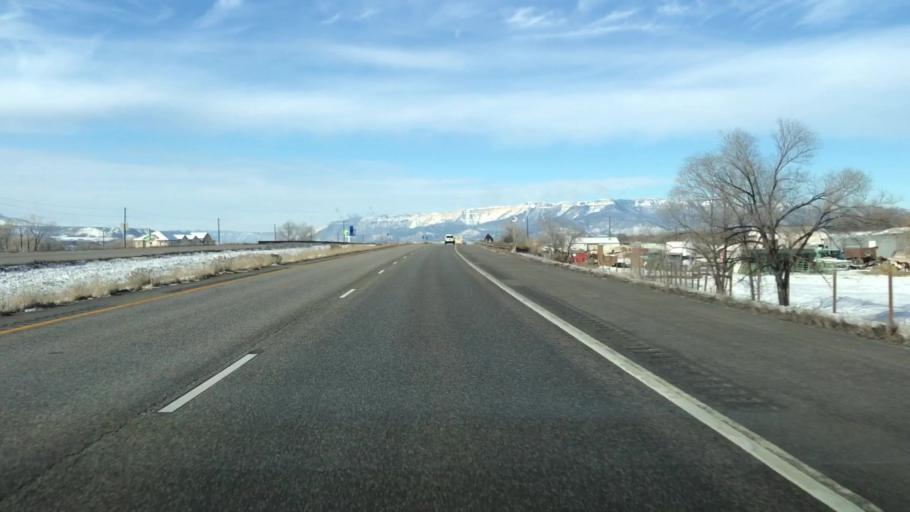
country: US
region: Colorado
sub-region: Garfield County
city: Silt
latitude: 39.5441
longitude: -107.6423
